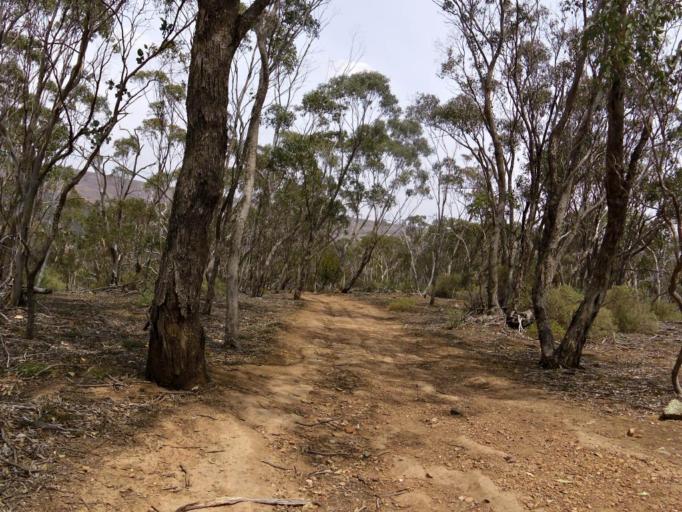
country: AU
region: Victoria
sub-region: Moorabool
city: Bacchus Marsh
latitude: -37.6677
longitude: 144.3655
